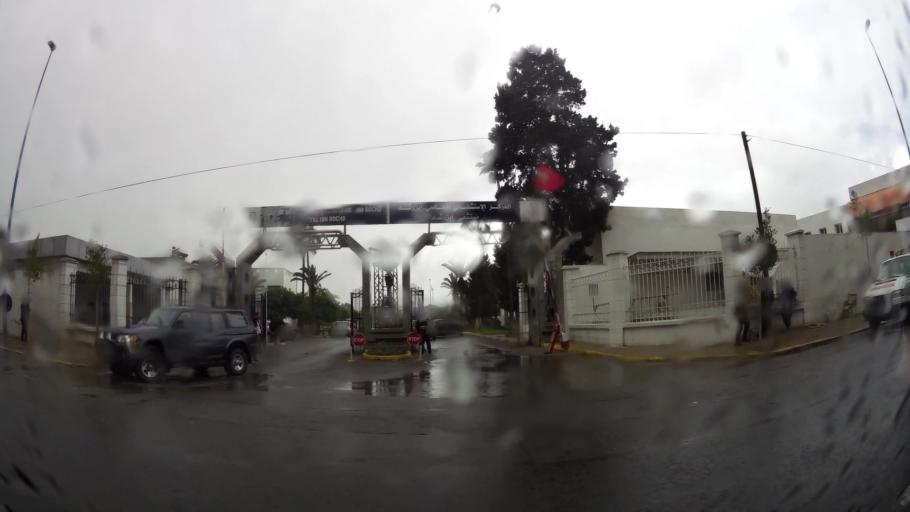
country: MA
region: Grand Casablanca
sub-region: Casablanca
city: Casablanca
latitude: 33.5787
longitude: -7.6176
